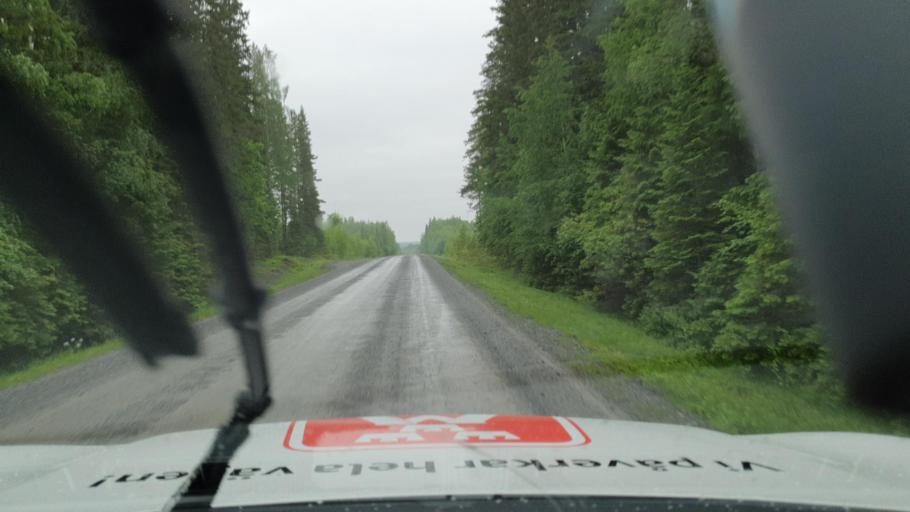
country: SE
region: Vaesterbotten
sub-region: Nordmalings Kommun
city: Nordmaling
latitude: 63.8302
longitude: 19.4881
